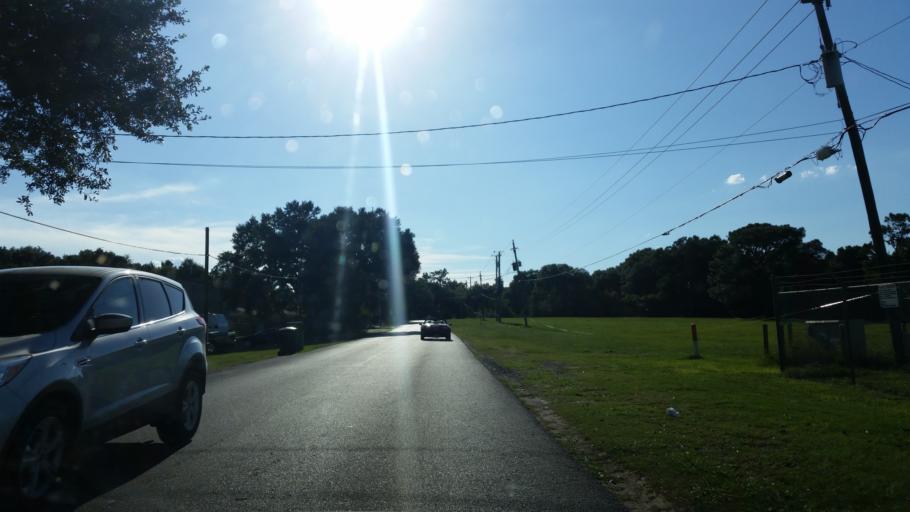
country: US
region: Florida
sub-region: Escambia County
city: Gonzalez
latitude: 30.5875
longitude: -87.2618
